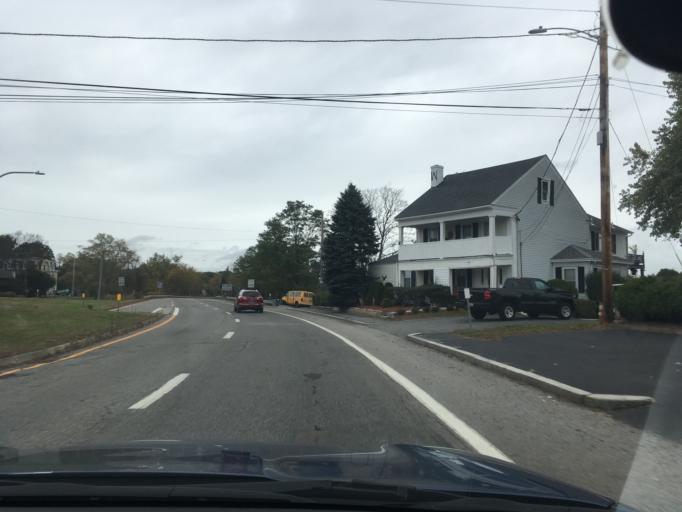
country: US
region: Rhode Island
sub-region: Bristol County
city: Barrington
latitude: 41.7516
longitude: -71.3211
